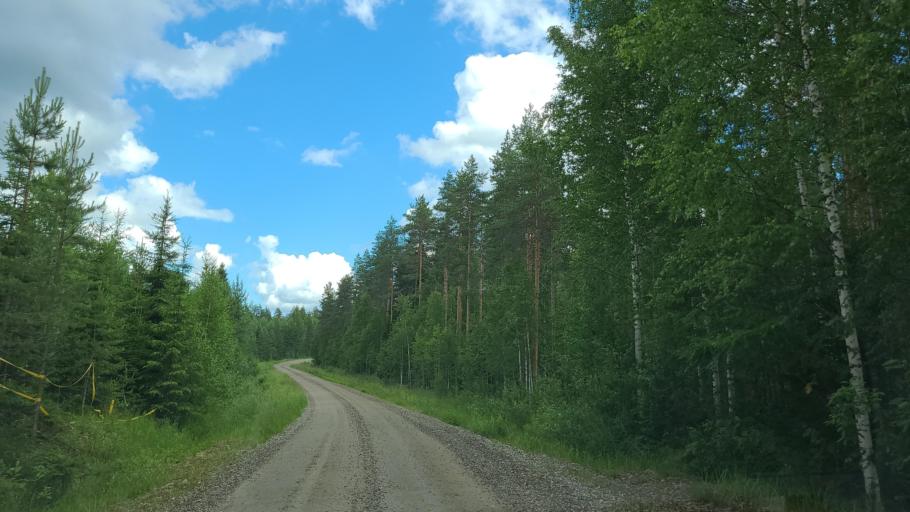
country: FI
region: Northern Savo
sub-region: Koillis-Savo
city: Kaavi
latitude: 63.0364
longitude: 28.7994
